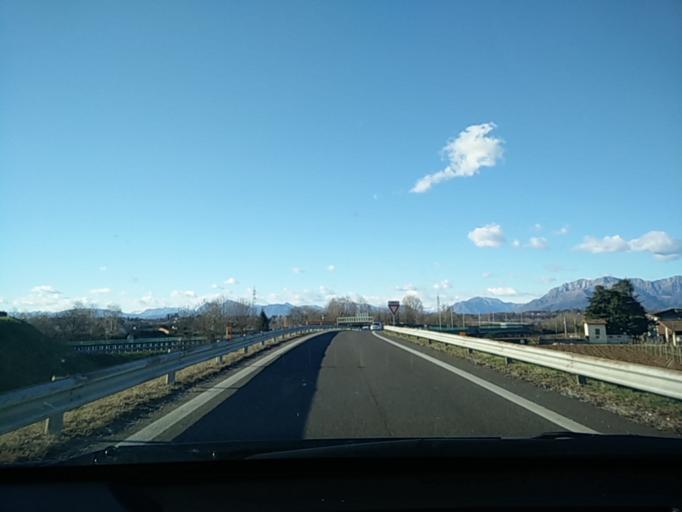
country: IT
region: Friuli Venezia Giulia
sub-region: Provincia di Udine
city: Tavagnacco
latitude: 46.1134
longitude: 13.2065
